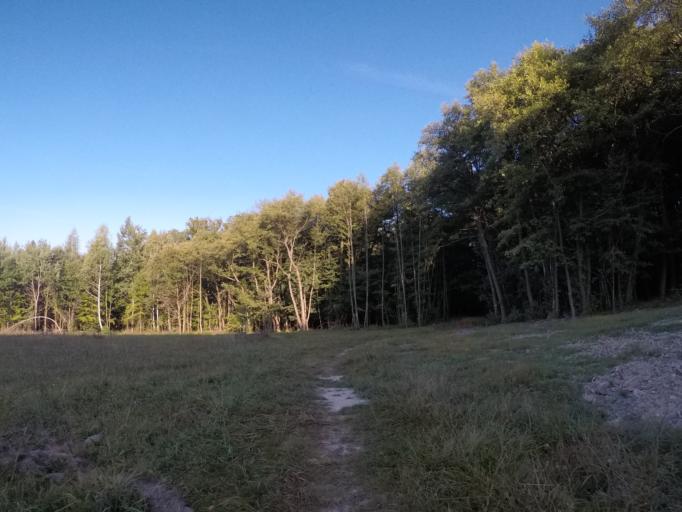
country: SK
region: Kosicky
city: Kosice
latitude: 48.7534
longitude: 21.1626
